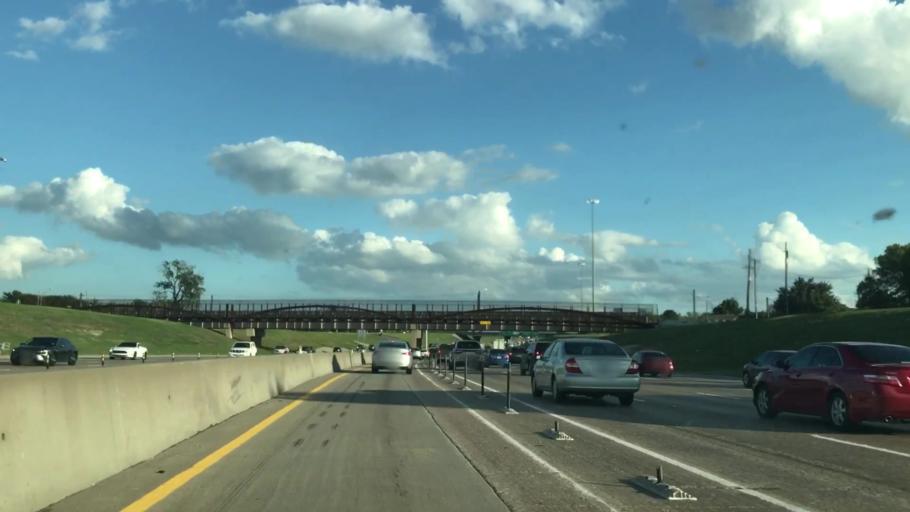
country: US
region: Texas
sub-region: Dallas County
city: Richardson
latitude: 32.8986
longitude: -96.7153
